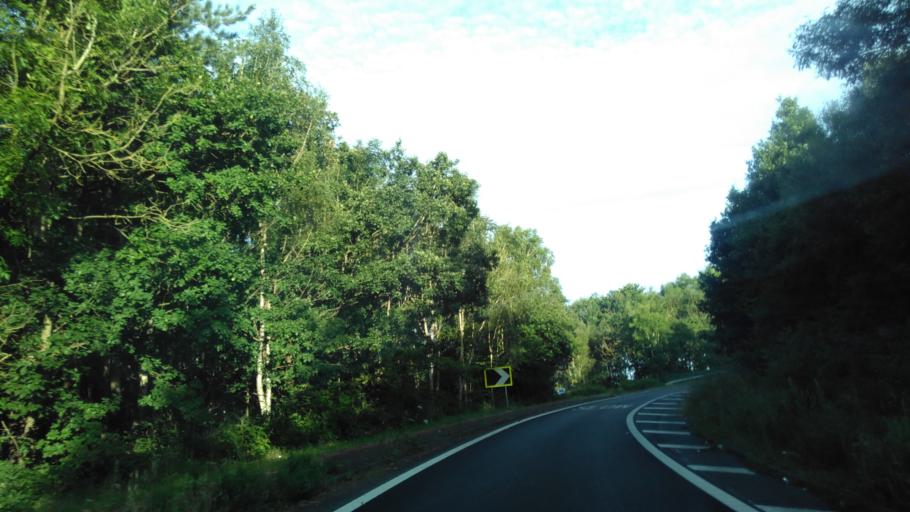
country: GB
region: England
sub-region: Kent
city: Dunkirk
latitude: 51.2886
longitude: 0.9827
